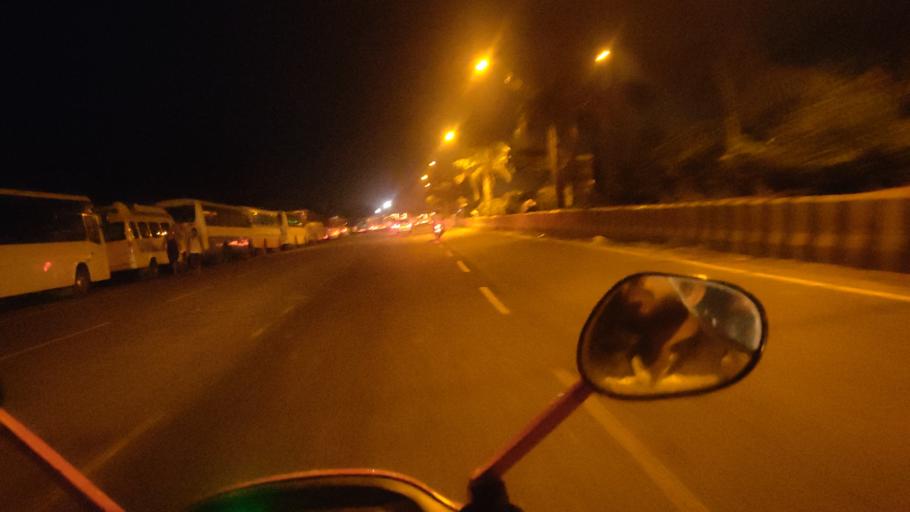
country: IN
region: Maharashtra
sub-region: Thane
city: Bhayandar
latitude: 19.2956
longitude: 72.8414
